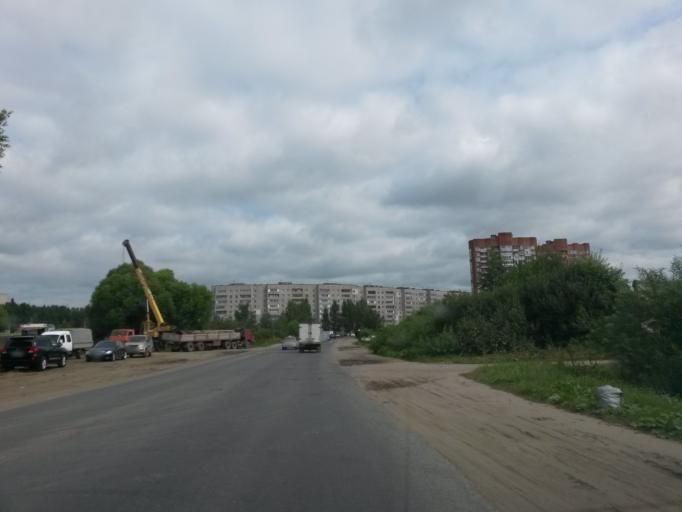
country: RU
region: Jaroslavl
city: Yaroslavl
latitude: 57.5678
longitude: 39.8594
